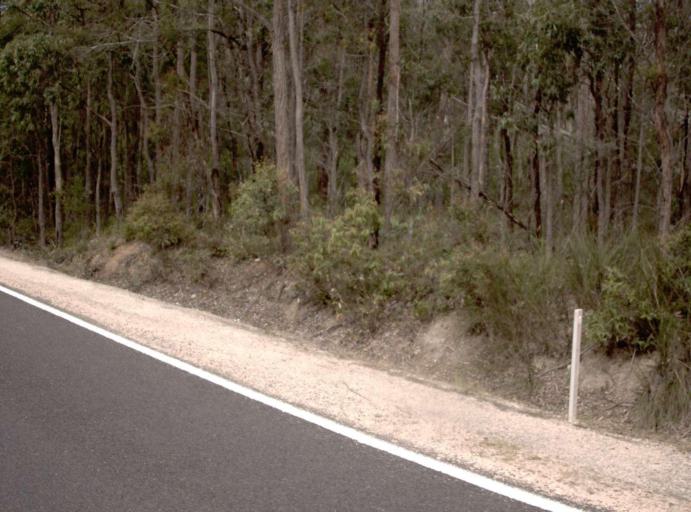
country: AU
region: New South Wales
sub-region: Bega Valley
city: Eden
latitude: -37.4416
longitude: 149.6432
